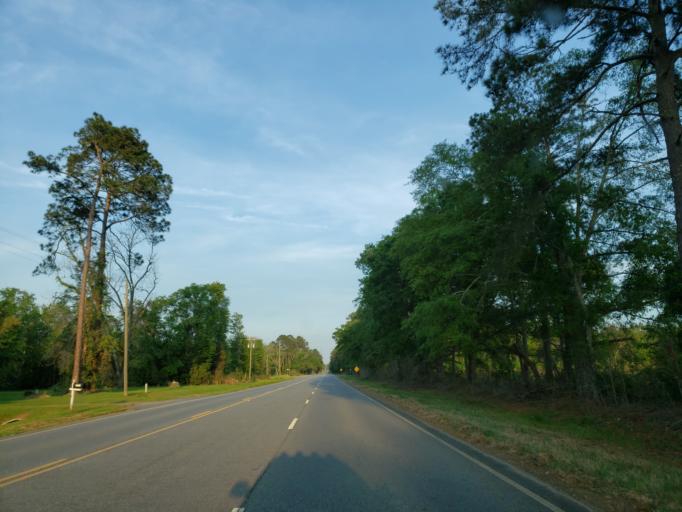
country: US
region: Georgia
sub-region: Lowndes County
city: Hahira
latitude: 30.9952
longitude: -83.4148
